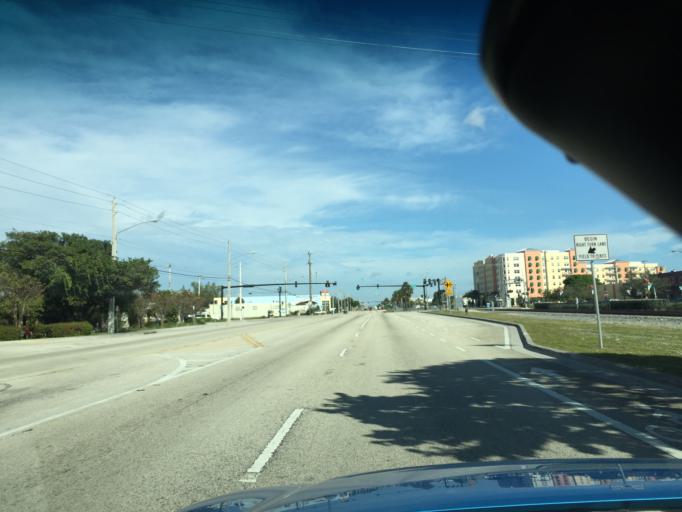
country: US
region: Florida
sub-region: Broward County
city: Pompano Beach
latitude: 26.2334
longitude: -80.1243
